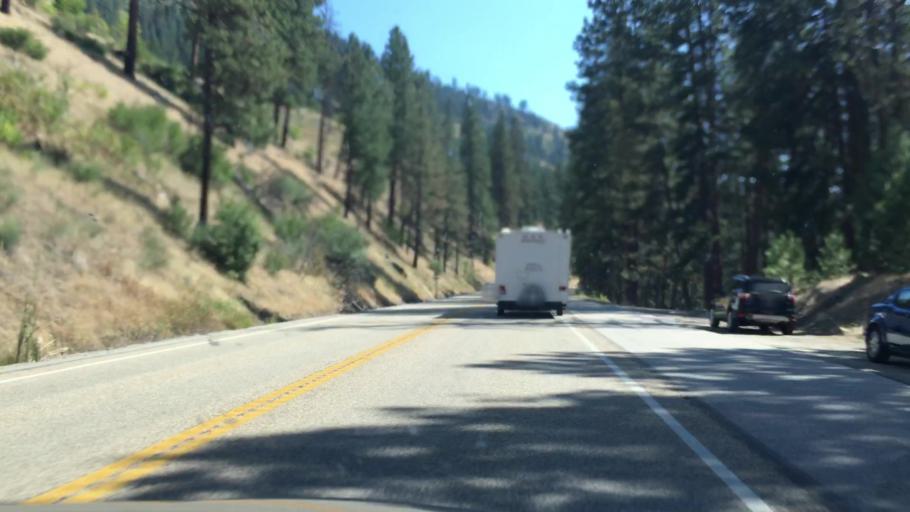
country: US
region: Idaho
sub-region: Boise County
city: Idaho City
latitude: 44.0714
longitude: -116.1185
